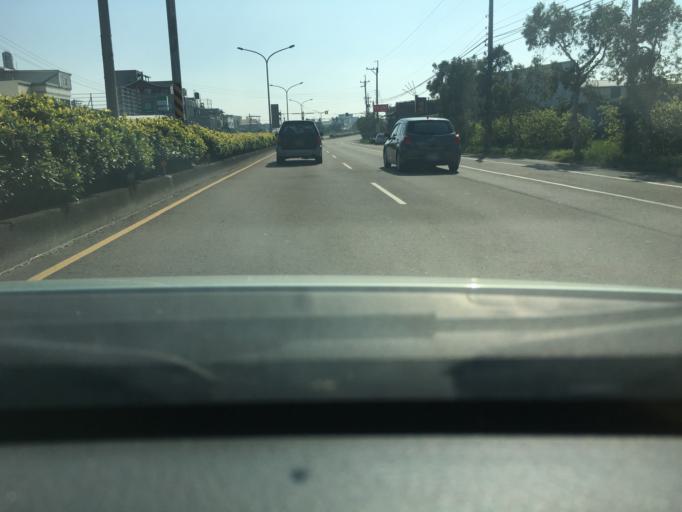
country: TW
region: Taiwan
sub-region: Hsinchu
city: Hsinchu
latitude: 24.8139
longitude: 120.9224
